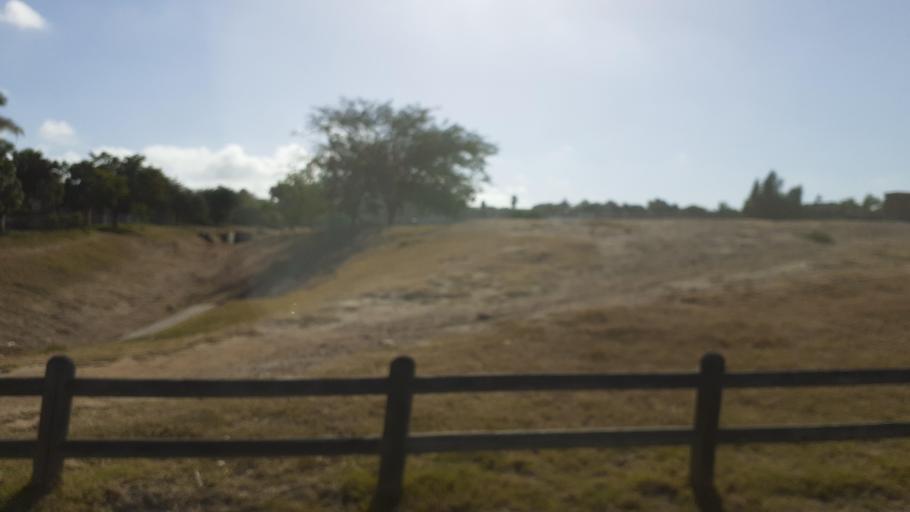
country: ZA
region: Western Cape
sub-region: City of Cape Town
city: Kraaifontein
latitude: -33.8154
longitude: 18.6910
